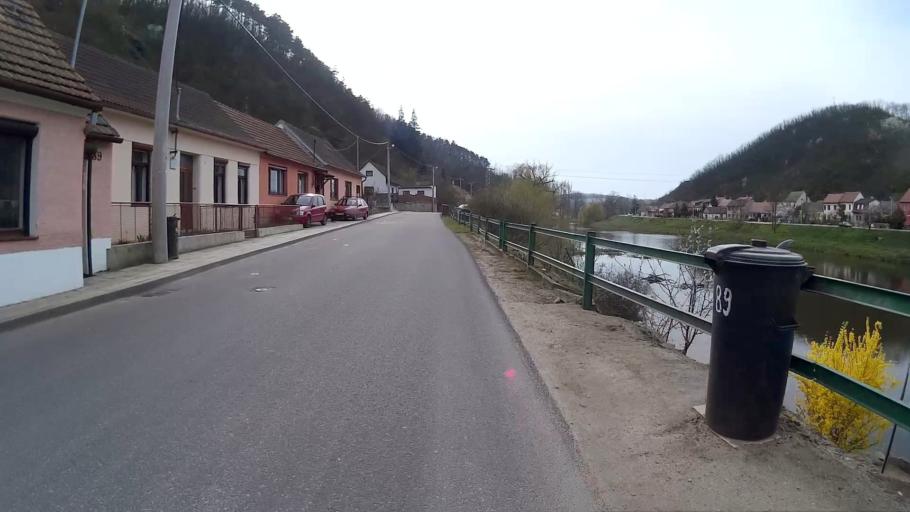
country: CZ
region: South Moravian
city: Dolni Kounice
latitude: 49.0705
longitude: 16.4588
